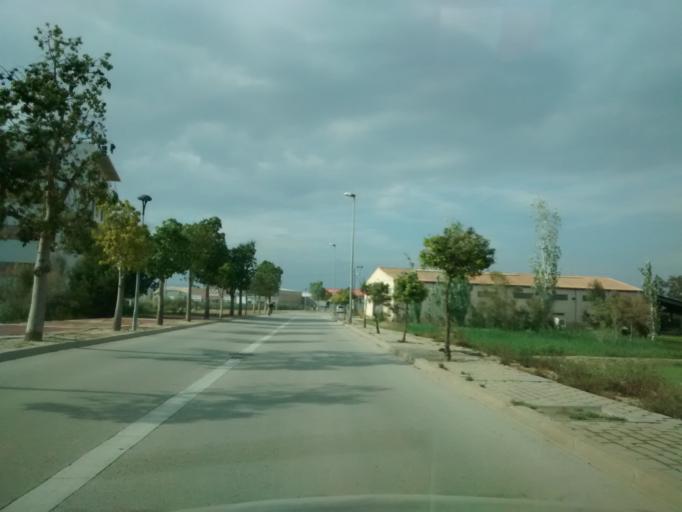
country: ES
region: Catalonia
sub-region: Provincia de Tarragona
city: Deltebre
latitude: 40.7226
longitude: 0.7209
